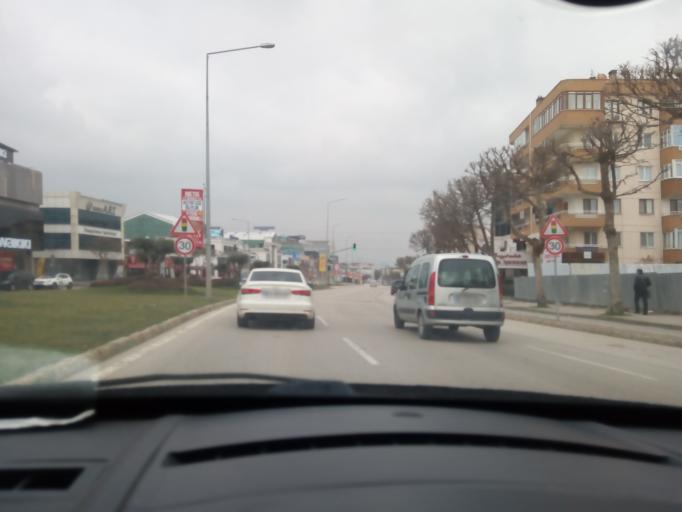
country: TR
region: Bursa
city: Yildirim
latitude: 40.2278
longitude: 28.9804
